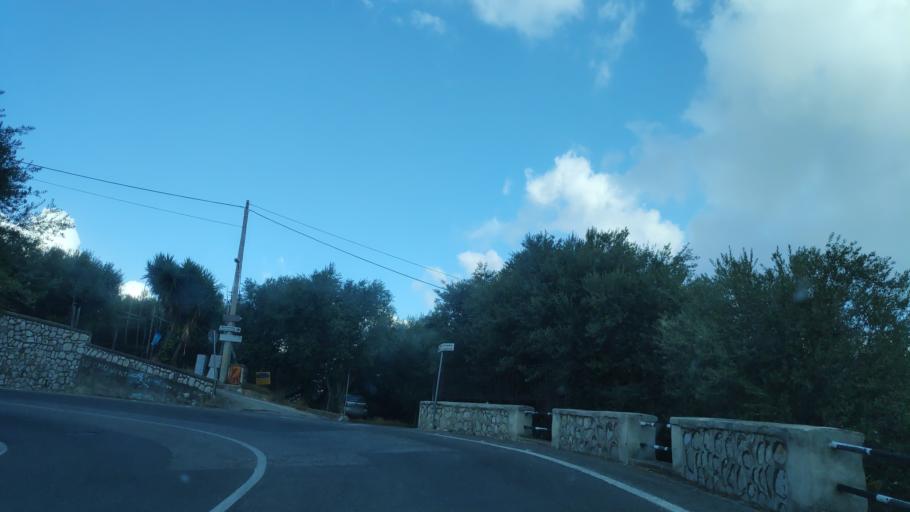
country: IT
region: Campania
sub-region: Provincia di Napoli
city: Piano di Sorrento
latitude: 40.6215
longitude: 14.4156
